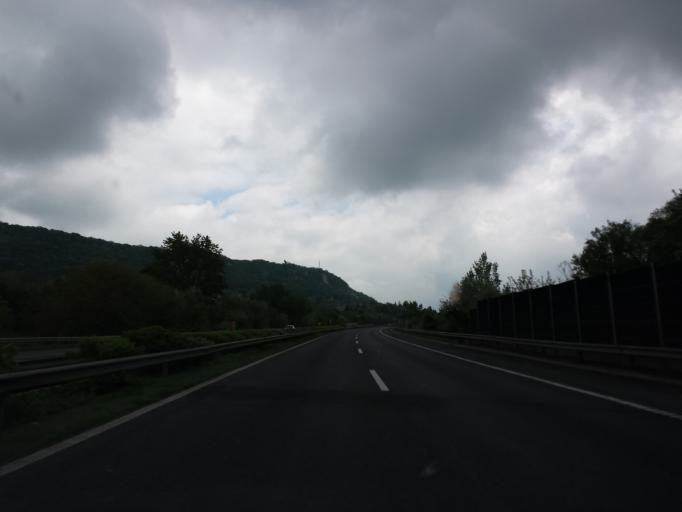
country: HU
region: Komarom-Esztergom
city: Tatabanya
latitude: 47.5949
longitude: 18.3957
